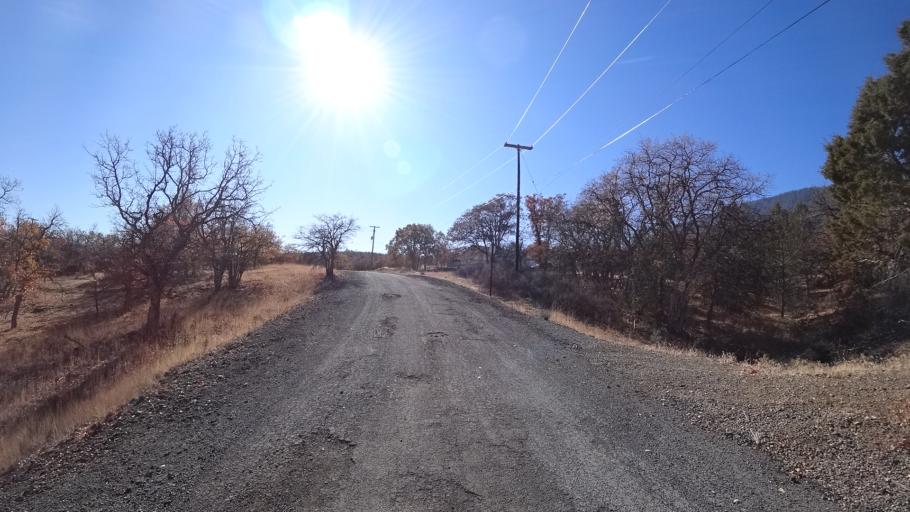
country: US
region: California
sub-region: Siskiyou County
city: Montague
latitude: 41.8744
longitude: -122.4805
